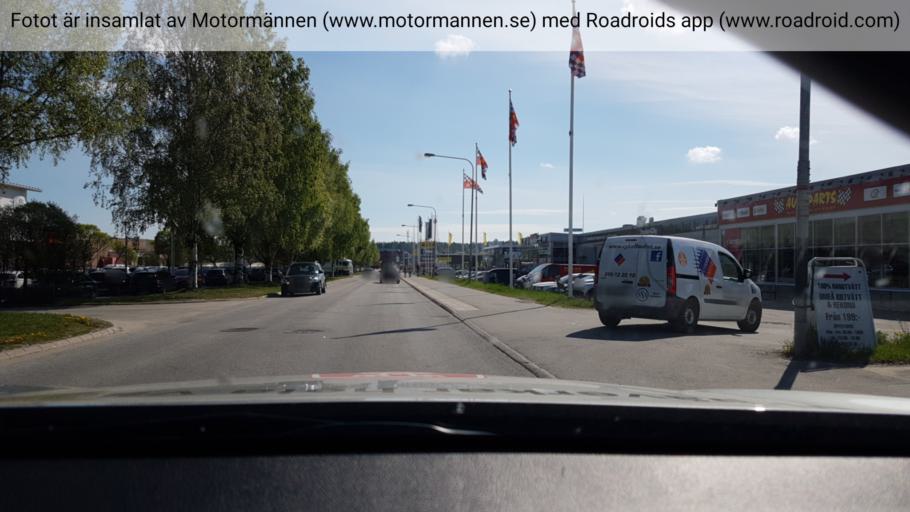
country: SE
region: Vaesterbotten
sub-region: Umea Kommun
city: Ersmark
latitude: 63.8512
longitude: 20.3049
